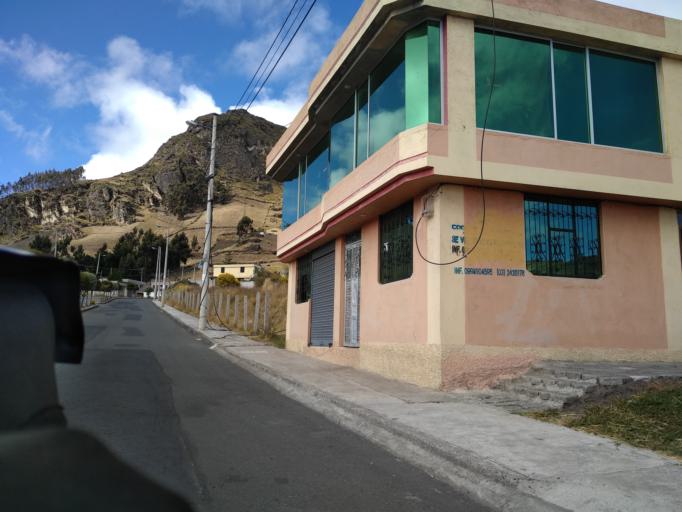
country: EC
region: Cotopaxi
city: Pujili
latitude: -0.9634
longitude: -78.9015
